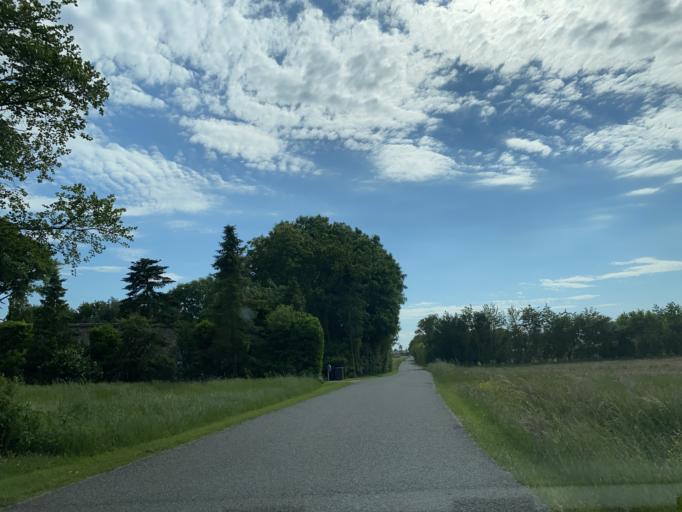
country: DK
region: Central Jutland
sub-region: Favrskov Kommune
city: Hammel
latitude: 56.2089
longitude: 9.8827
